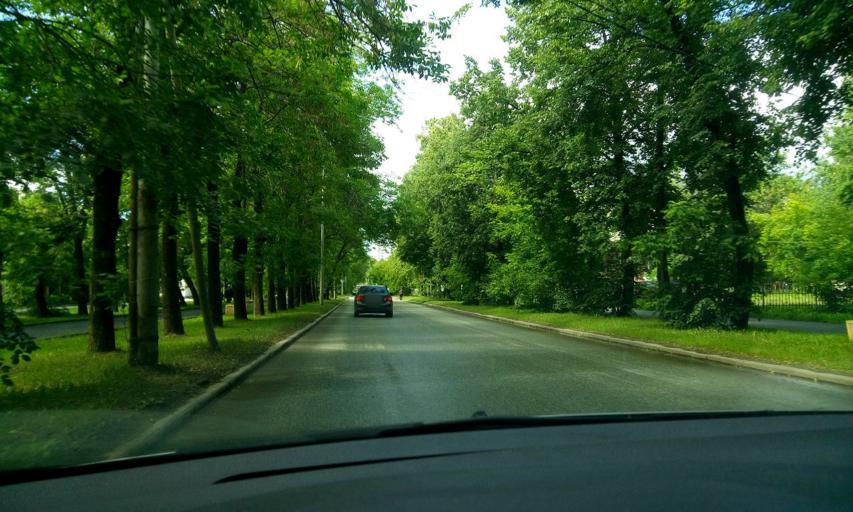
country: RU
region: Sverdlovsk
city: Yekaterinburg
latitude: 56.8887
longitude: 60.6020
